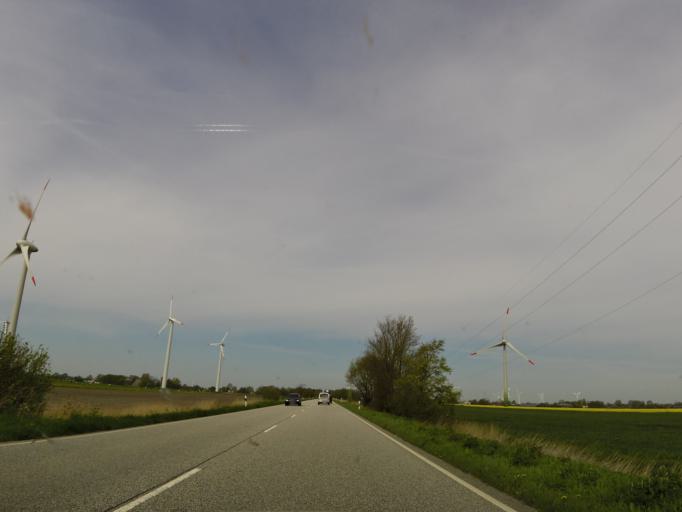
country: DE
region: Schleswig-Holstein
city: Hemme
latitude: 54.2687
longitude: 9.0215
